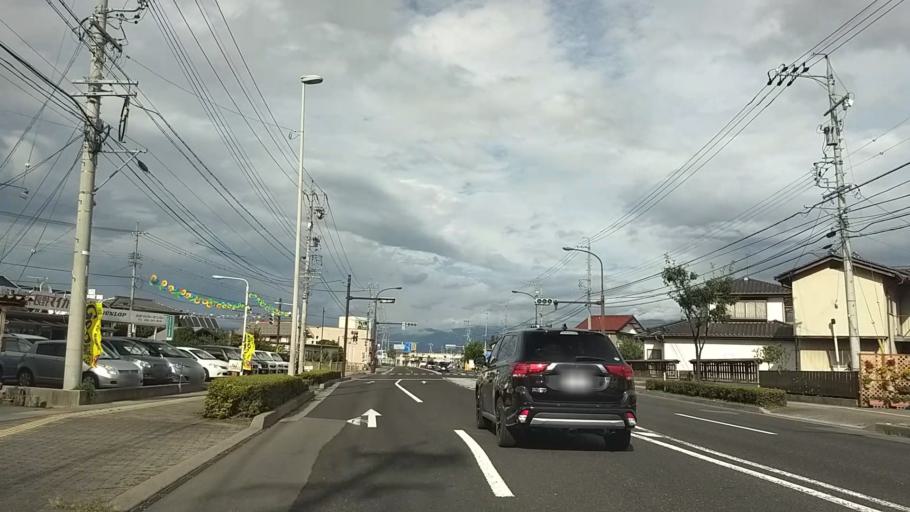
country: JP
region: Nagano
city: Suzaka
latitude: 36.6590
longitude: 138.2540
